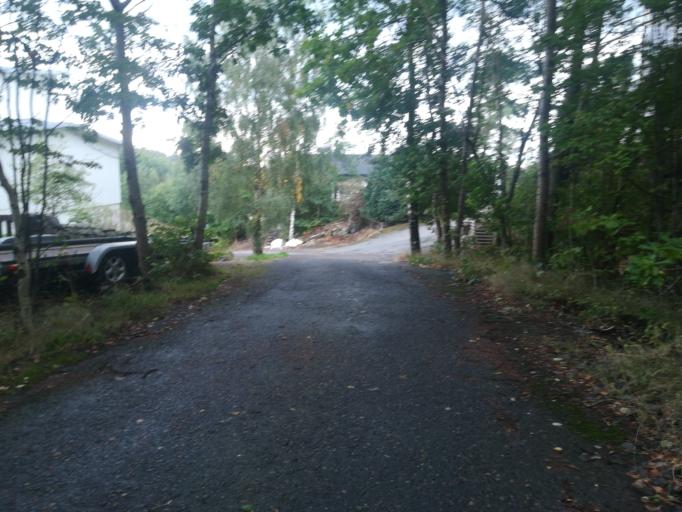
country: SE
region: Vaestra Goetaland
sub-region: Goteborg
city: Billdal
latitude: 57.6197
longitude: 11.9511
